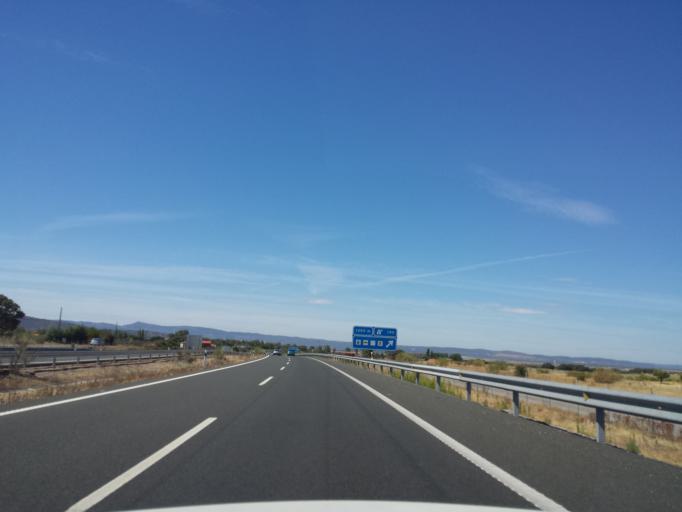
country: ES
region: Extremadura
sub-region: Provincia de Caceres
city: Millanes
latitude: 39.8613
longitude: -5.6106
